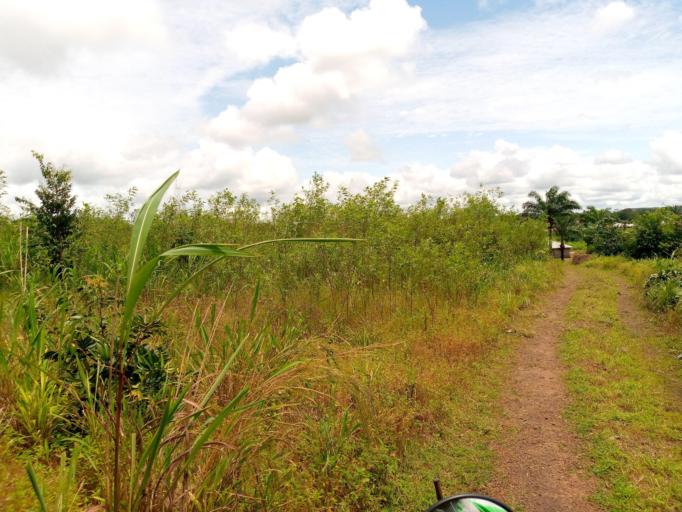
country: SL
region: Northern Province
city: Magburaka
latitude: 8.7190
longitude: -11.9261
